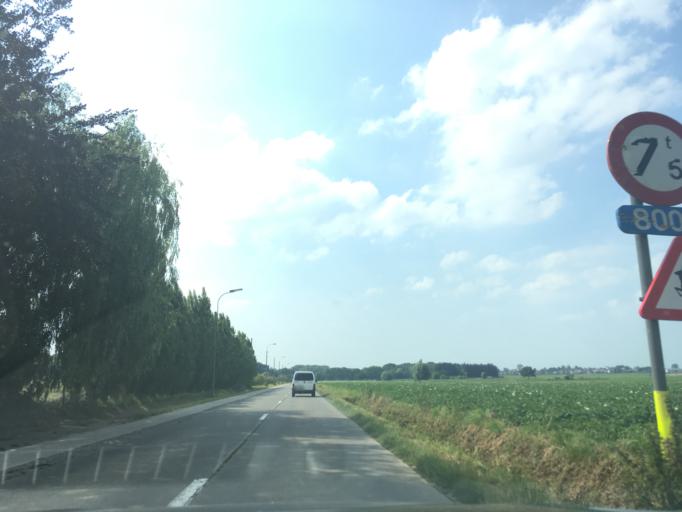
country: BE
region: Flanders
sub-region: Provincie West-Vlaanderen
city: Houthulst
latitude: 50.9715
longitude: 2.9703
